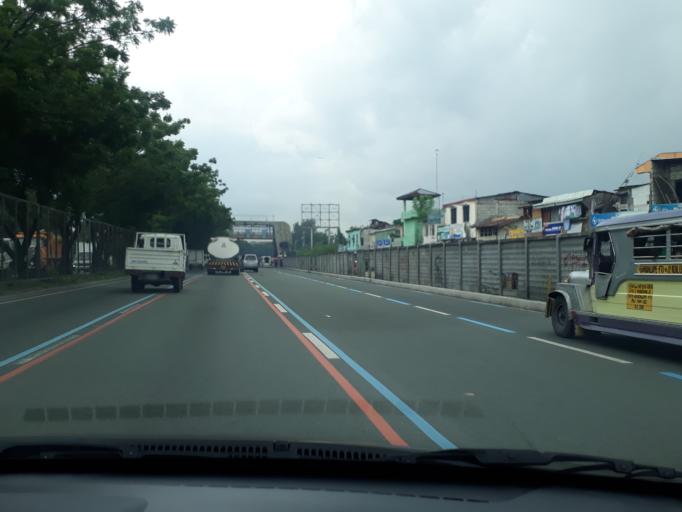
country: PH
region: Calabarzon
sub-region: Province of Rizal
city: Pateros
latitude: 14.5244
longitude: 121.0551
